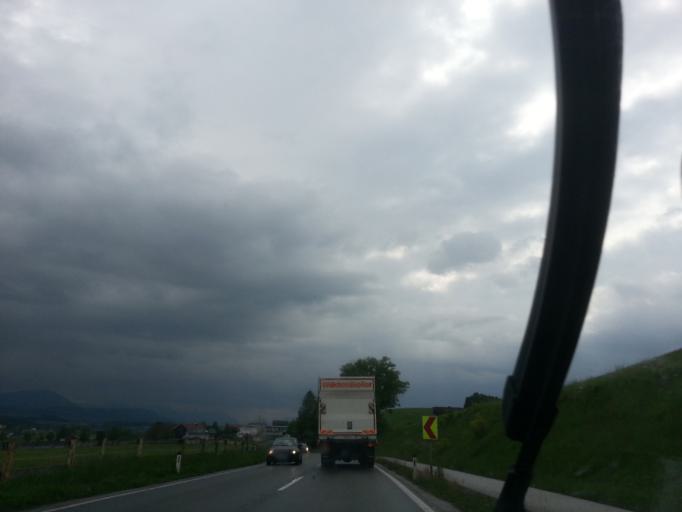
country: AT
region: Salzburg
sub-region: Politischer Bezirk Salzburg-Umgebung
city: Kostendorf
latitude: 47.9200
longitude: 13.2096
